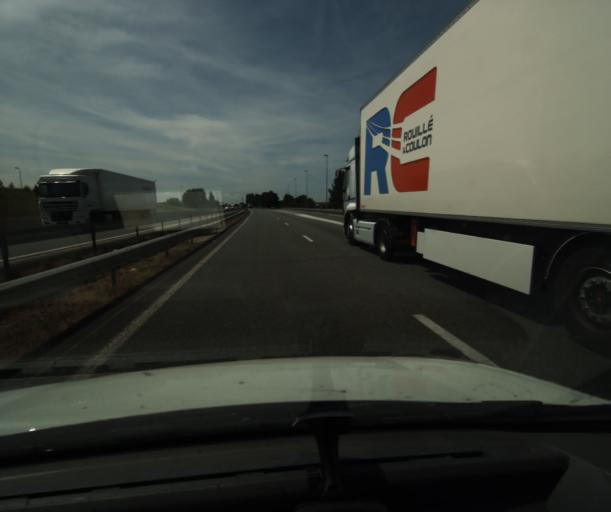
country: FR
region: Languedoc-Roussillon
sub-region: Departement de l'Aude
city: Arzens
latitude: 43.2180
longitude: 2.2215
